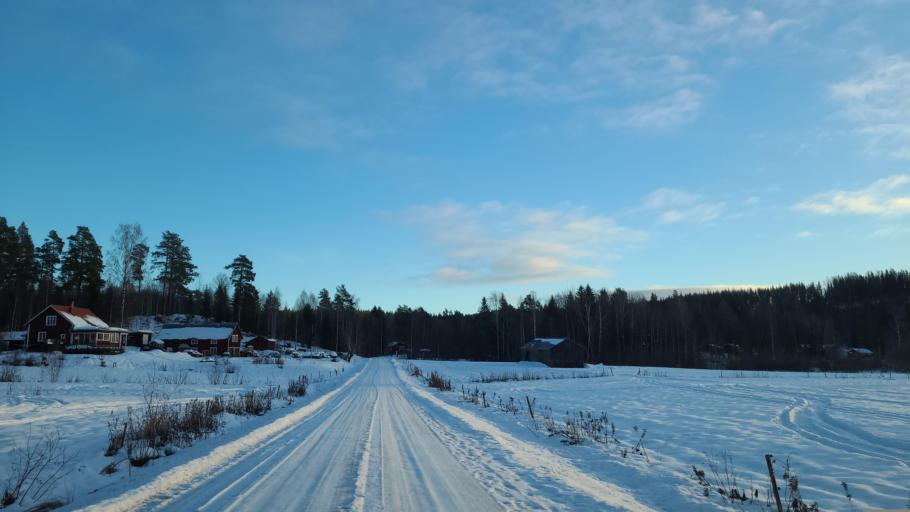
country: SE
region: Gaevleborg
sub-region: Bollnas Kommun
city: Kilafors
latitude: 61.3950
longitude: 16.6851
